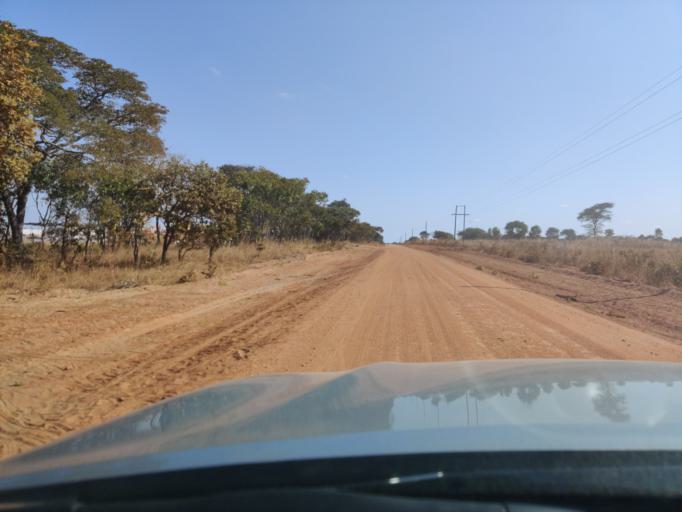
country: ZM
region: Central
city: Mkushi
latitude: -13.9912
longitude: 29.5303
